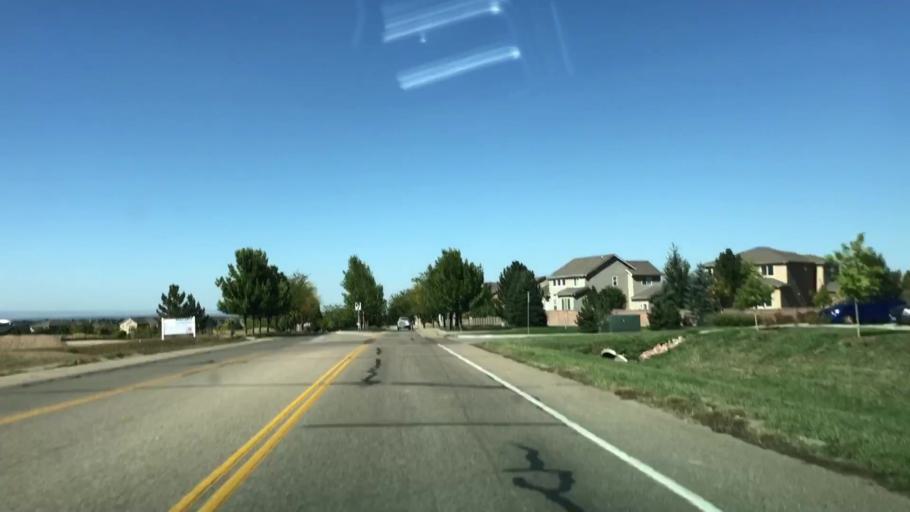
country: US
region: Colorado
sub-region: Weld County
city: Windsor
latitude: 40.4395
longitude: -104.9676
